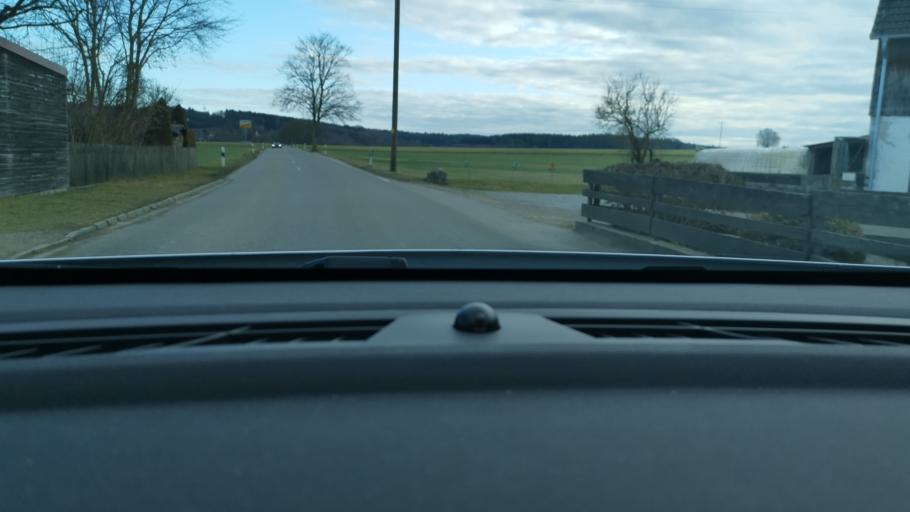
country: DE
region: Bavaria
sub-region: Swabia
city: Affing
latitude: 48.4972
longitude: 11.0010
